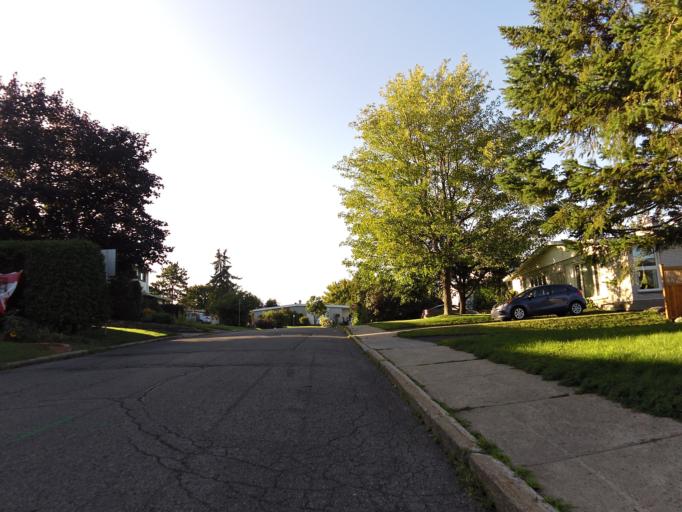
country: CA
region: Ontario
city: Ottawa
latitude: 45.3558
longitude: -75.7255
